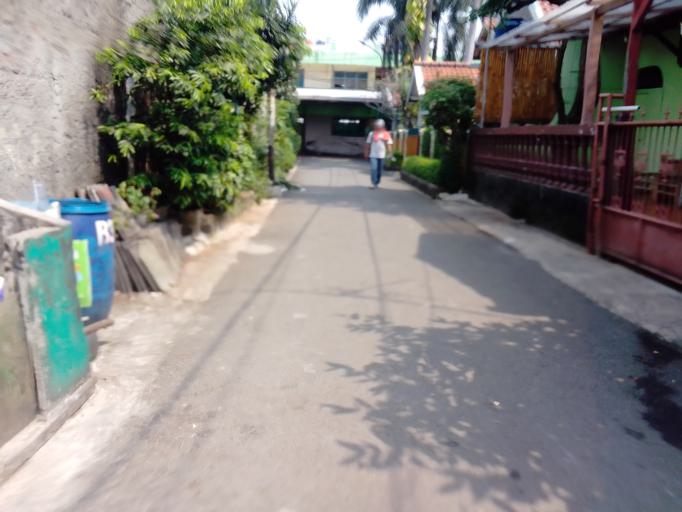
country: ID
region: Jakarta Raya
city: Jakarta
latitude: -6.2179
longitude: 106.7941
